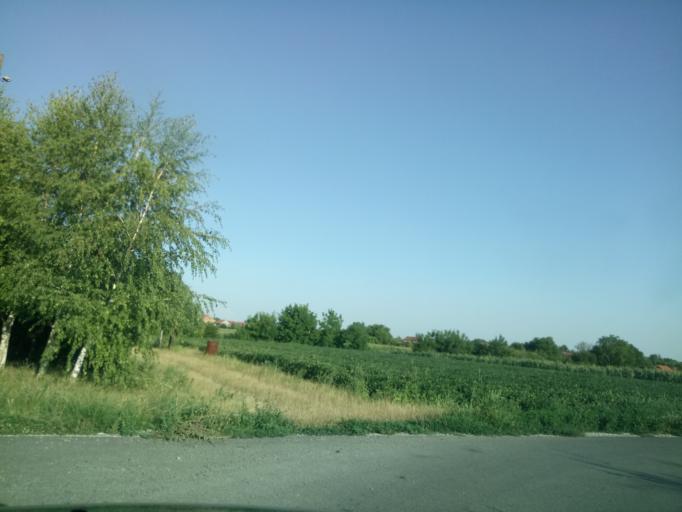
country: RS
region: Autonomna Pokrajina Vojvodina
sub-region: Sremski Okrug
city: Stara Pazova
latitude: 44.9923
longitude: 20.1729
